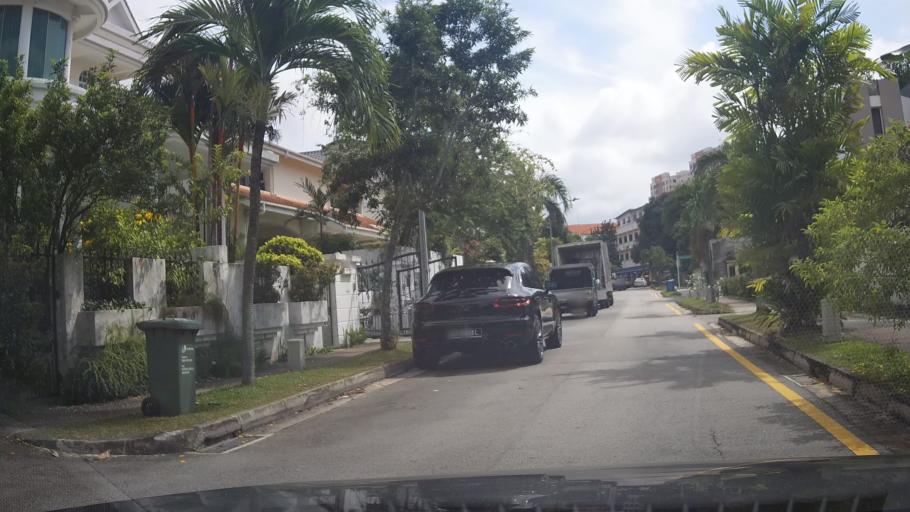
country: SG
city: Singapore
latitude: 1.3065
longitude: 103.8941
